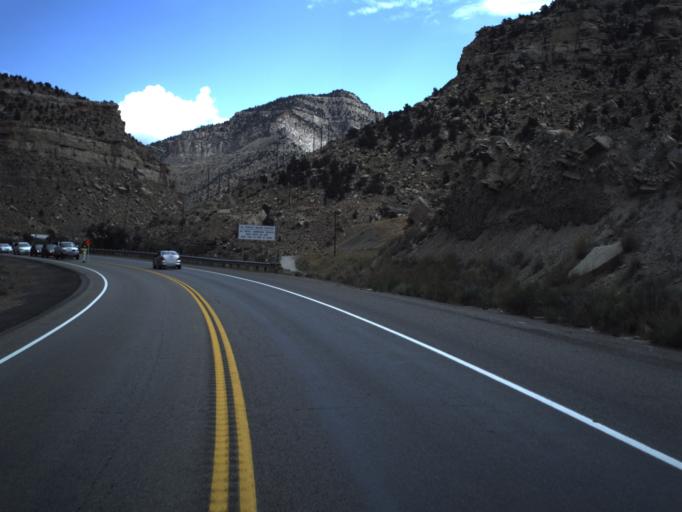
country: US
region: Utah
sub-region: Carbon County
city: Helper
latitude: 39.7117
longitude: -110.8677
